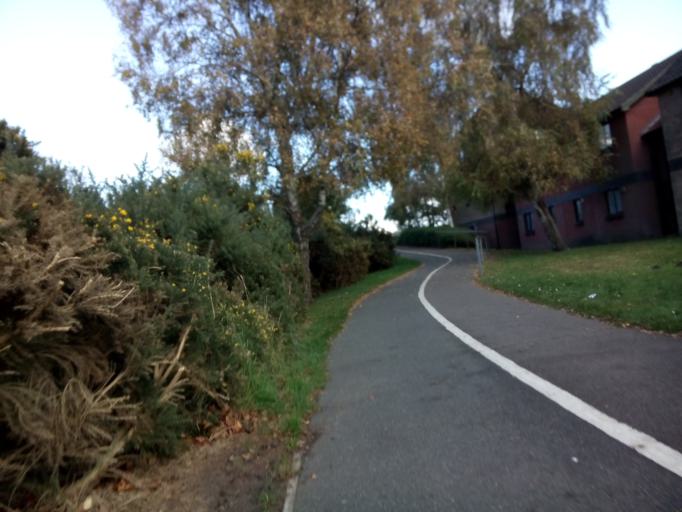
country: GB
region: England
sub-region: Suffolk
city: Kesgrave
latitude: 52.0612
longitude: 1.2751
